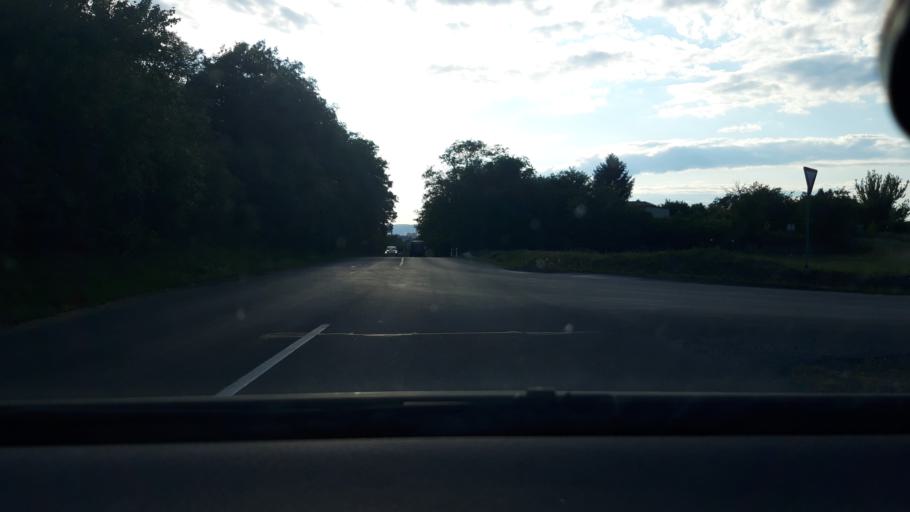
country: SK
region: Banskobystricky
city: Lucenec
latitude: 48.3267
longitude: 19.6950
